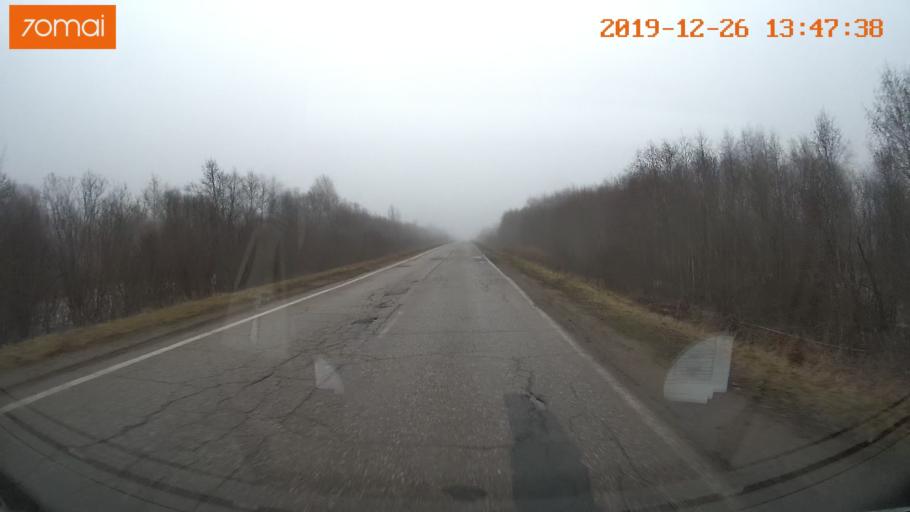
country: RU
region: Vologda
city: Sheksna
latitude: 58.6833
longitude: 38.5365
